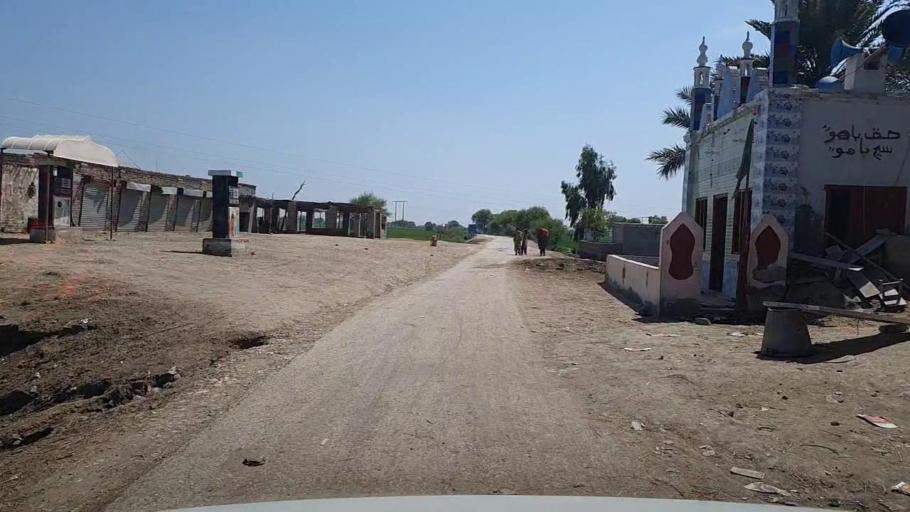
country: PK
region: Sindh
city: Kandhkot
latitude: 28.3187
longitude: 69.3400
